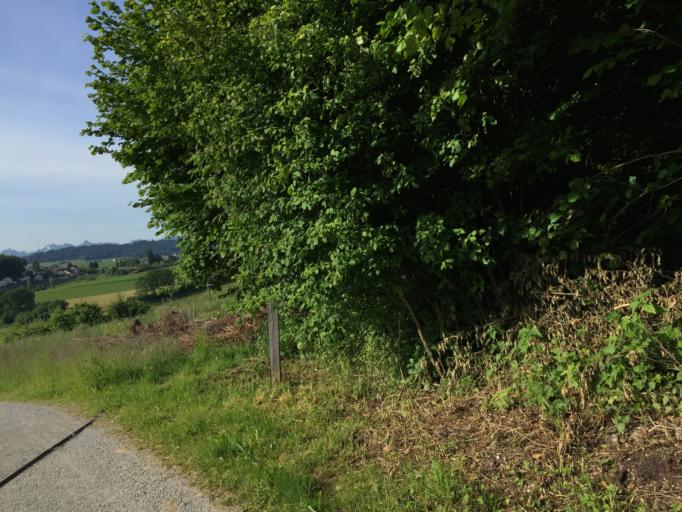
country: CH
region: Bern
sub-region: Bern-Mittelland District
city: Koniz
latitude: 46.9215
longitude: 7.4016
